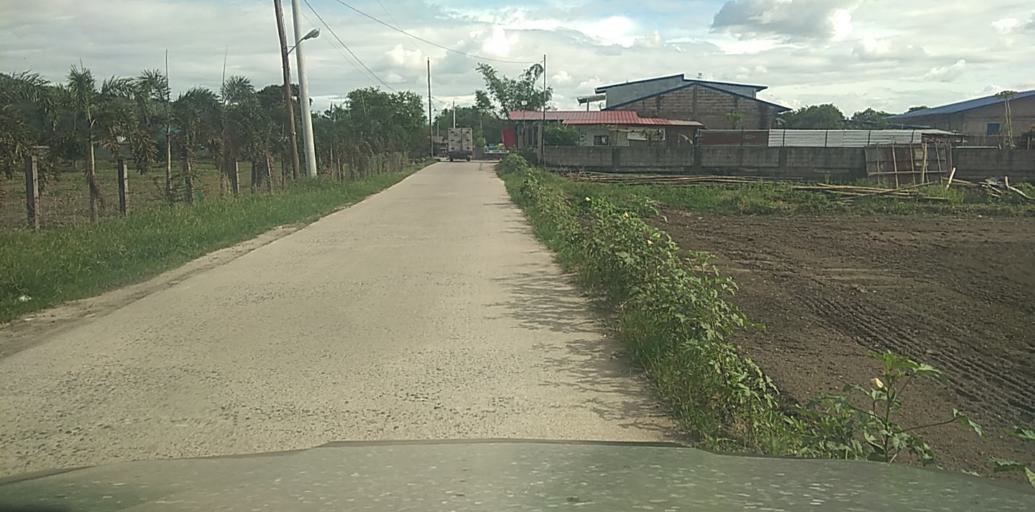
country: PH
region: Central Luzon
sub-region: Province of Pampanga
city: Panlinlang
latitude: 15.1860
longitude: 120.6941
